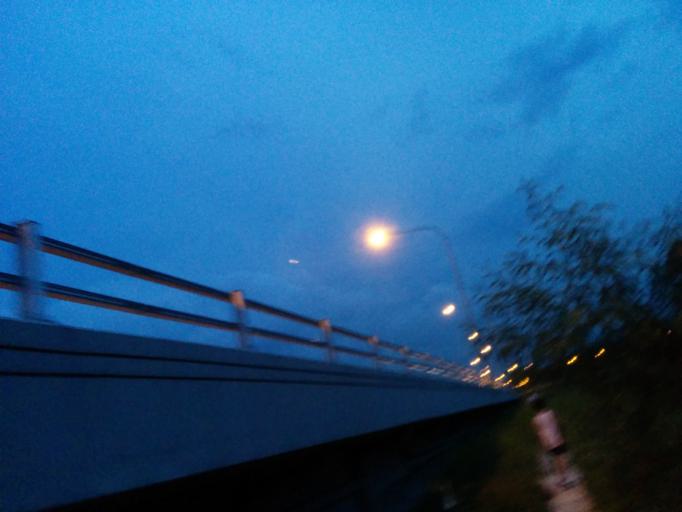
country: MY
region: Johor
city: Kampung Pasir Gudang Baru
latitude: 1.4016
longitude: 103.8852
